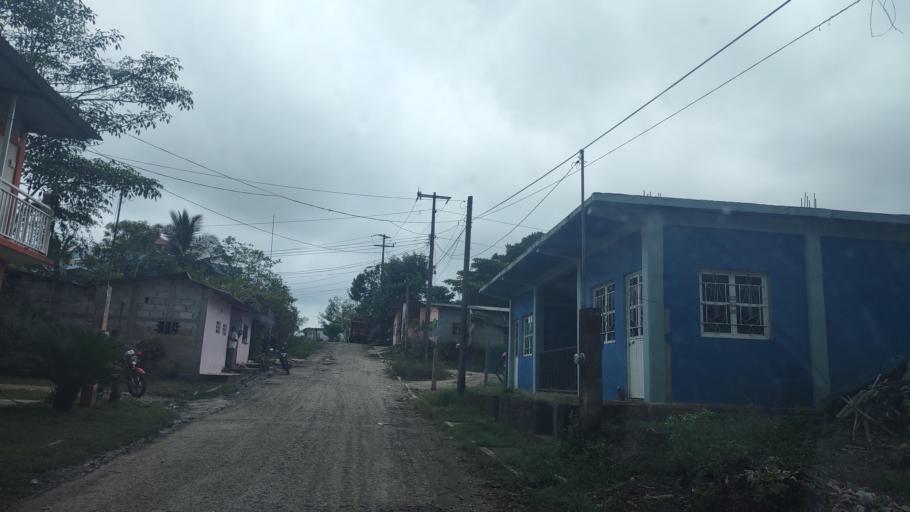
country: MX
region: Veracruz
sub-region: Uxpanapa
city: Poblado 10
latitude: 17.4950
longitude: -94.1615
